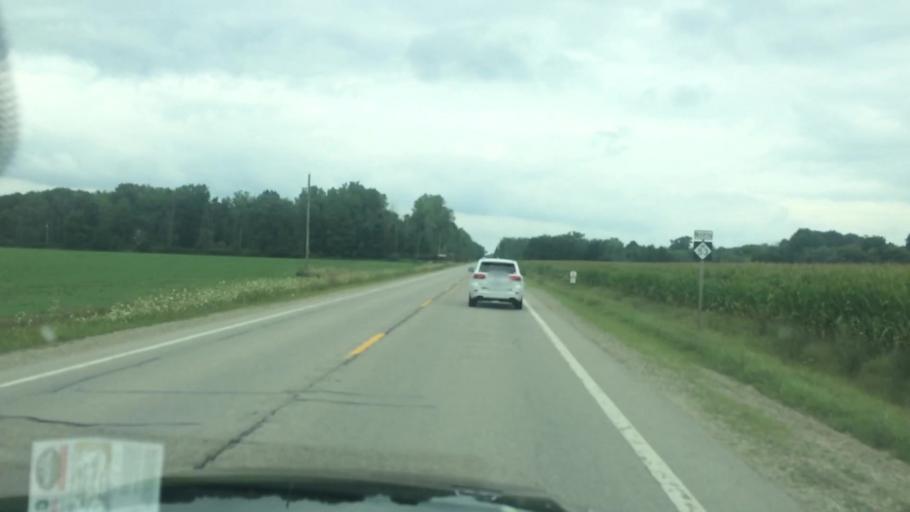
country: US
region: Michigan
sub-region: Tuscola County
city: Cass City
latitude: 43.4870
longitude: -83.0910
